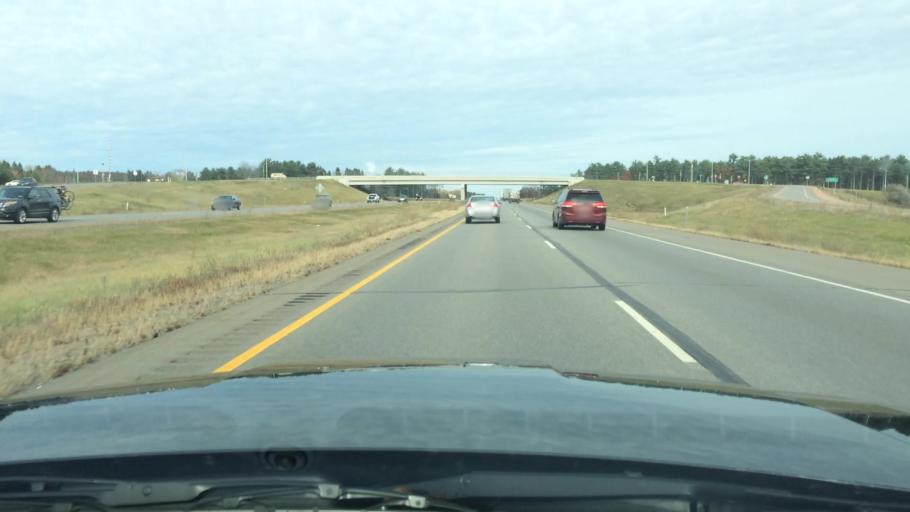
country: US
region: Wisconsin
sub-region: Marathon County
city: Mosinee
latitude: 44.8091
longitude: -89.6740
